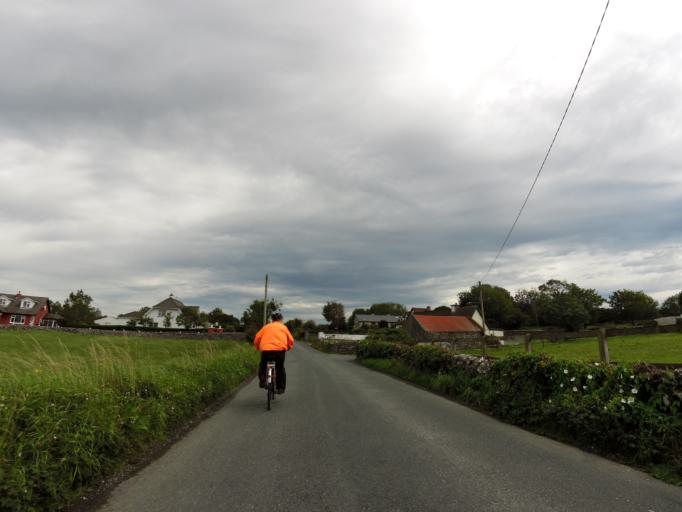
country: IE
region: Connaught
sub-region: County Galway
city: Gaillimh
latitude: 53.3147
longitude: -9.0352
